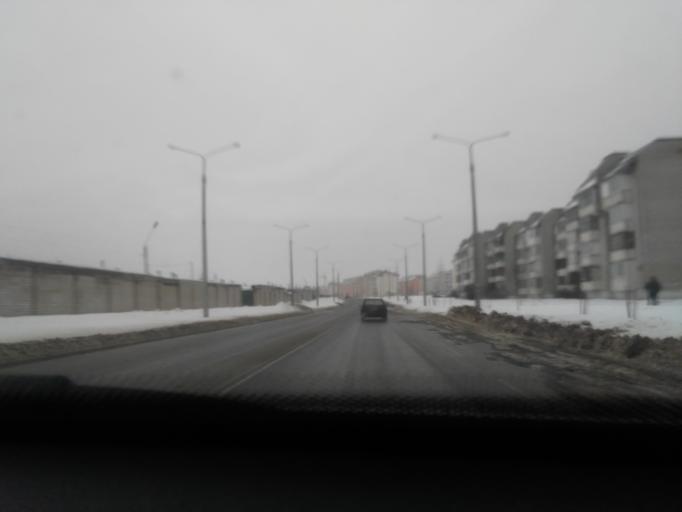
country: BY
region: Mogilev
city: Babruysk
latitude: 53.1917
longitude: 29.2206
